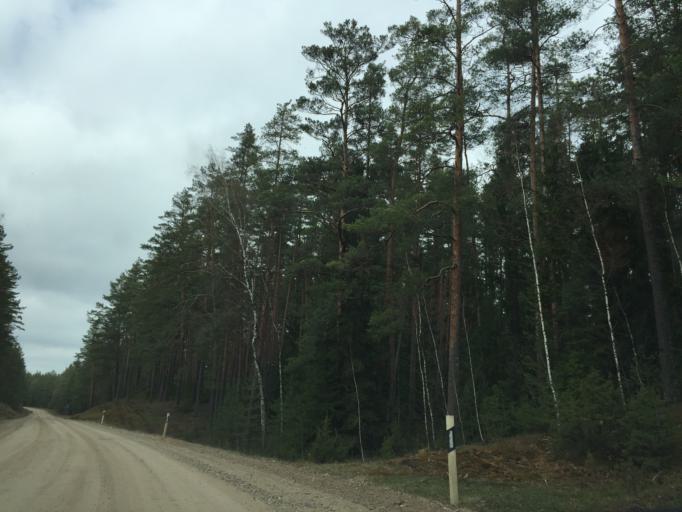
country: EE
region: Valgamaa
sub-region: Valga linn
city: Valga
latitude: 57.6628
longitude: 26.2010
